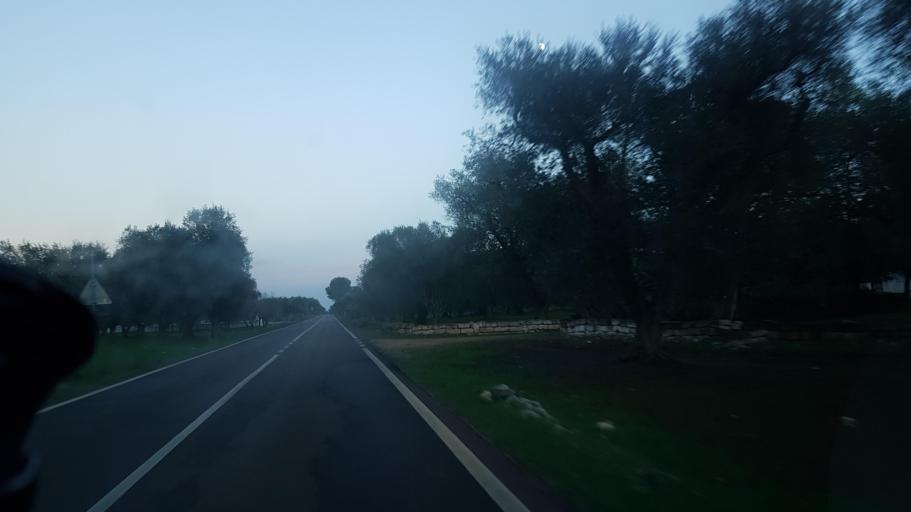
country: IT
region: Apulia
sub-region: Provincia di Brindisi
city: Latiano
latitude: 40.5695
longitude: 17.6665
